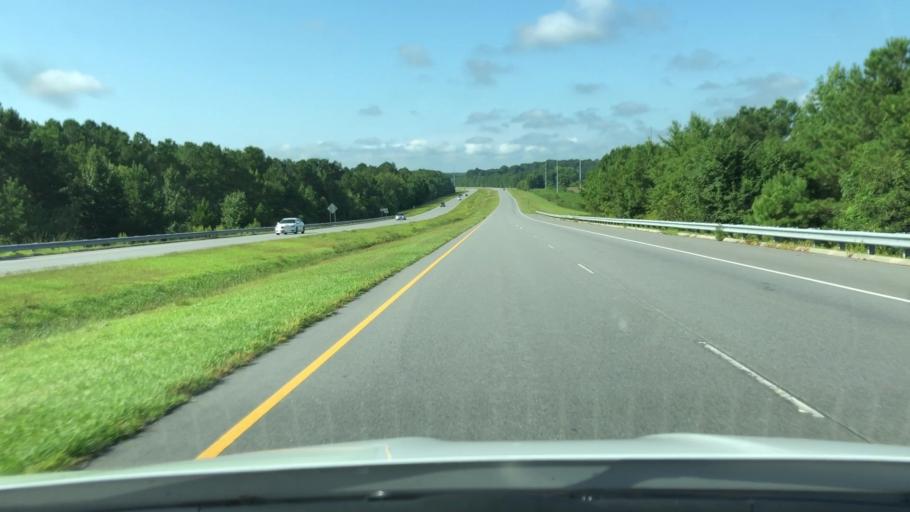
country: US
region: North Carolina
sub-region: Currituck County
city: Moyock
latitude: 36.4541
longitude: -76.3347
